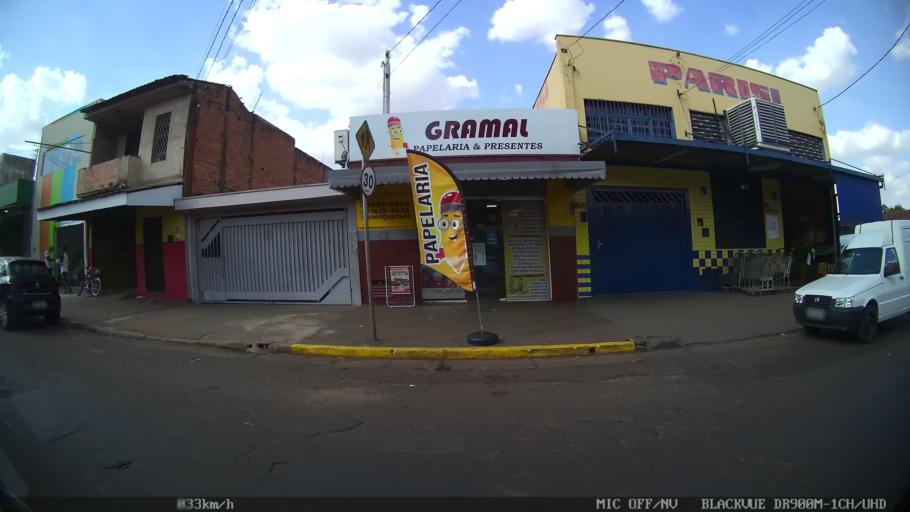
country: BR
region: Sao Paulo
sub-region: Ribeirao Preto
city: Ribeirao Preto
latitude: -21.1970
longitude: -47.8388
